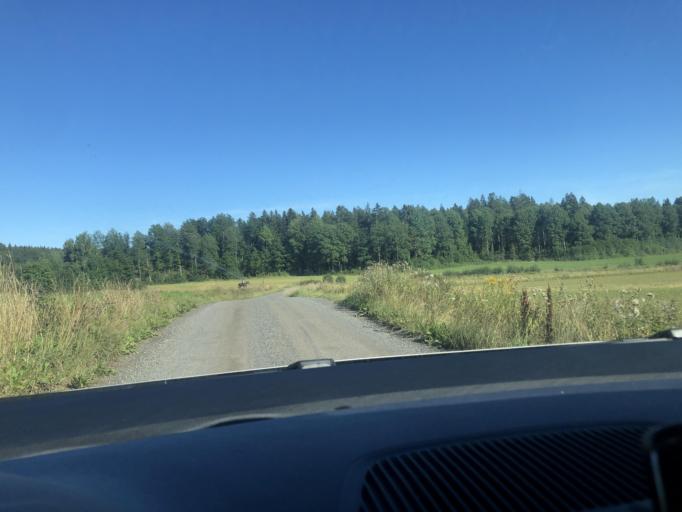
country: SE
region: Joenkoeping
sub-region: Jonkopings Kommun
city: Huskvarna
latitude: 57.7981
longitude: 14.3103
